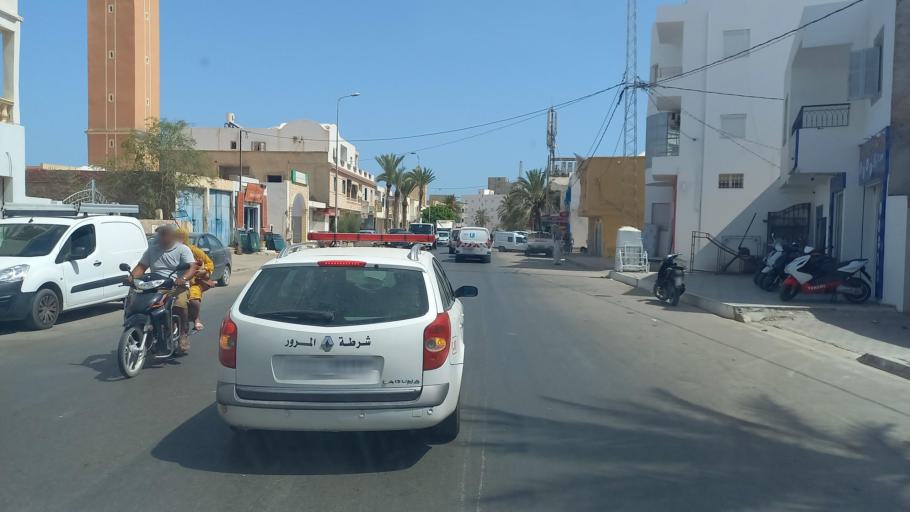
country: TN
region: Madanin
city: Zarzis
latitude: 33.4991
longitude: 11.0985
